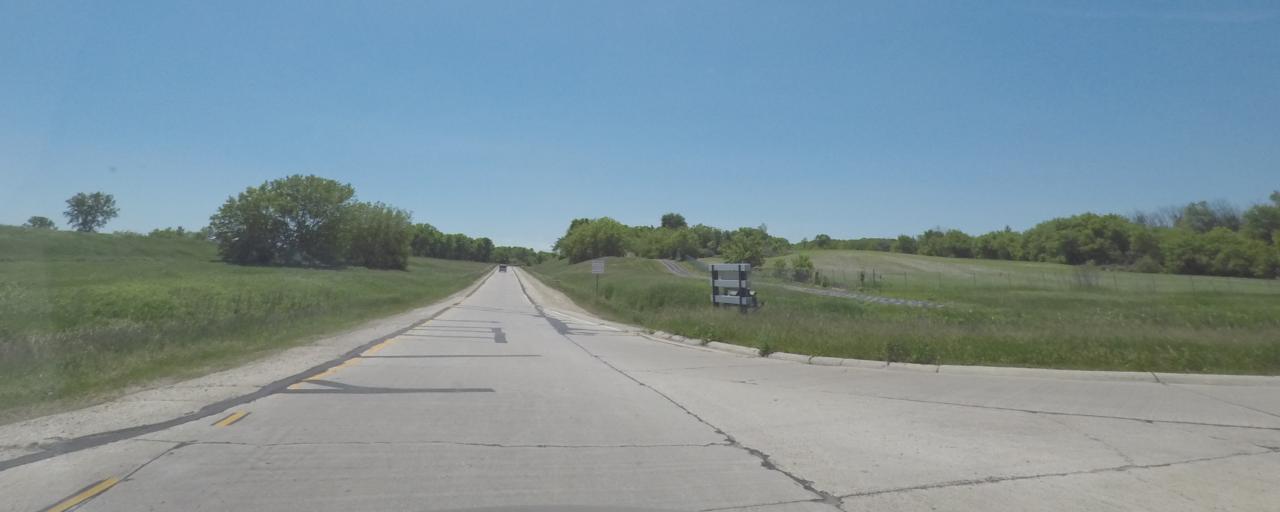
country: US
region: Wisconsin
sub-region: Washington County
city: West Bend
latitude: 43.4555
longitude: -88.2066
